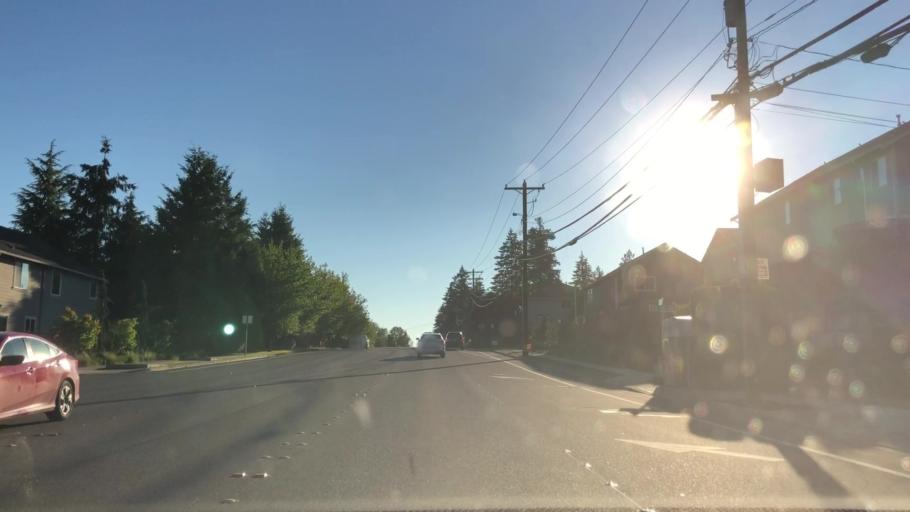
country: US
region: Washington
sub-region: Snohomish County
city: North Creek
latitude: 47.8346
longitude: -122.1875
